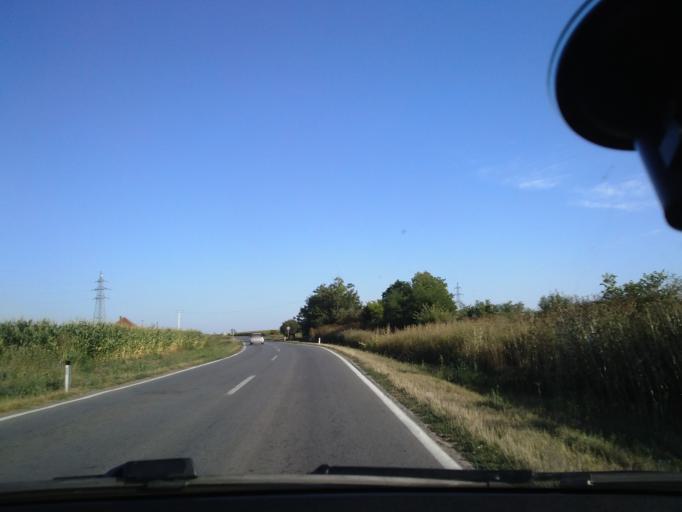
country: RS
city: Doroslovo
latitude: 45.6837
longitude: 19.1772
